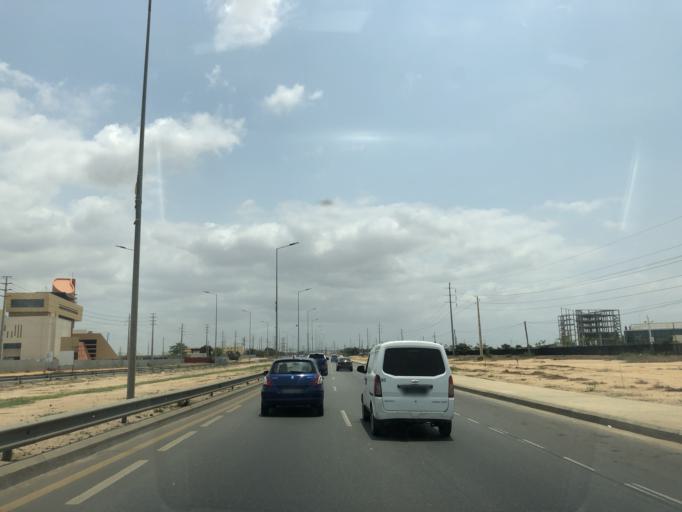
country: AO
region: Luanda
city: Luanda
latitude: -8.9601
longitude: 13.2569
